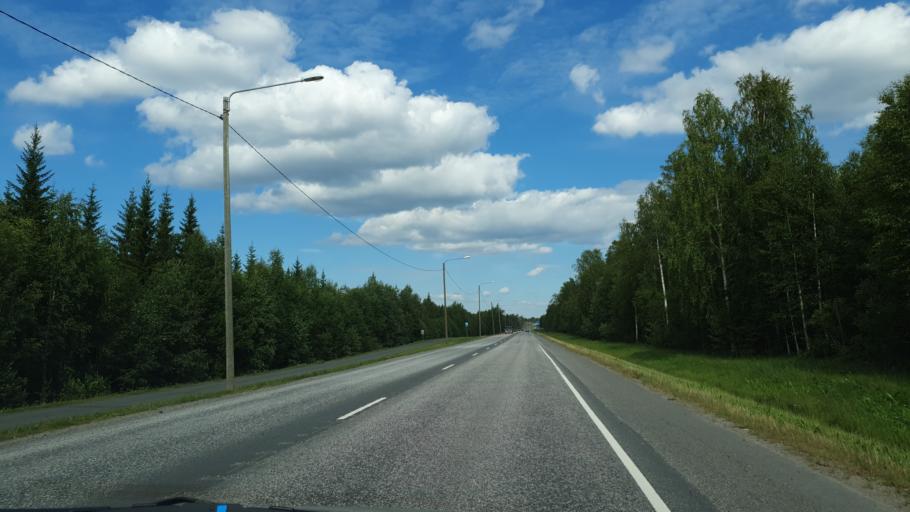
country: FI
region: Kainuu
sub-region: Kajaani
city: Kajaani
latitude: 64.2629
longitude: 27.8393
